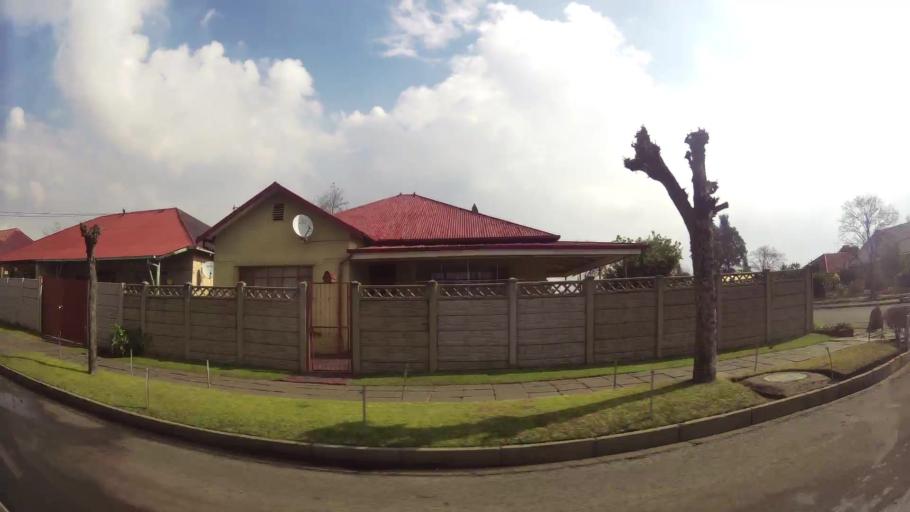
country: ZA
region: Gauteng
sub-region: Sedibeng District Municipality
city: Vereeniging
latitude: -26.6746
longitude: 27.9206
